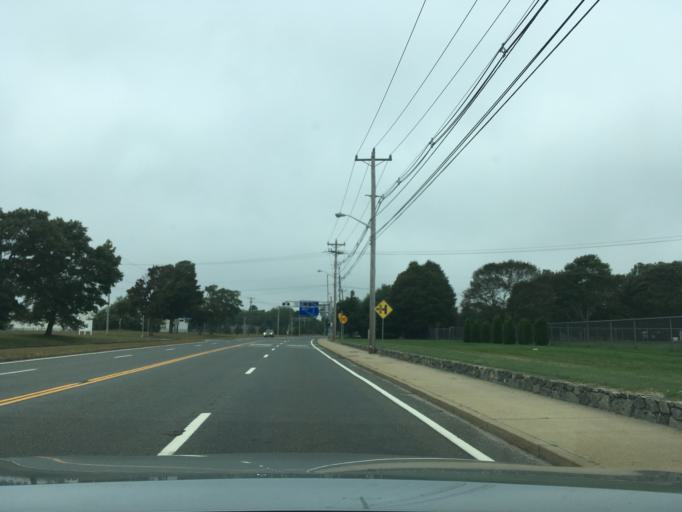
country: US
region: Rhode Island
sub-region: Washington County
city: North Kingstown
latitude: 41.5920
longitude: -71.4280
